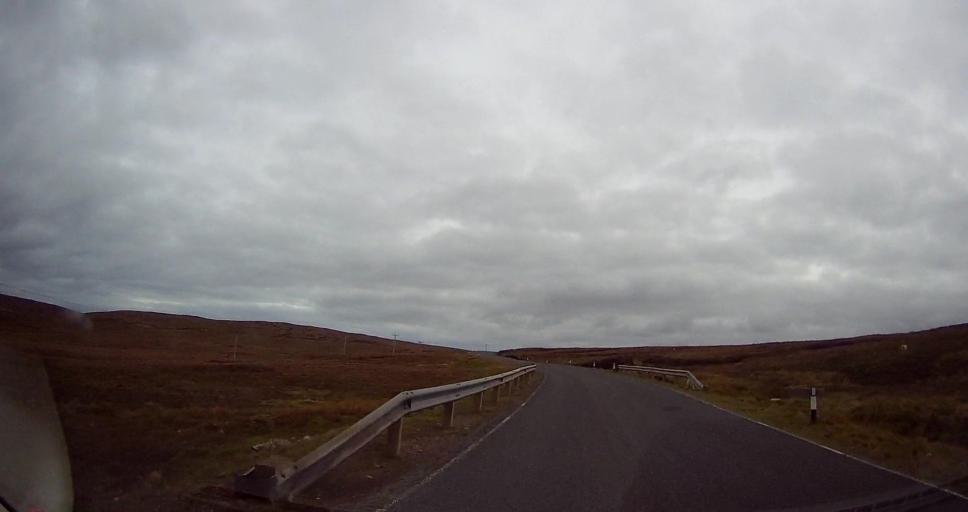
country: GB
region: Scotland
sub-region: Shetland Islands
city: Shetland
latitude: 60.6356
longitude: -1.0664
